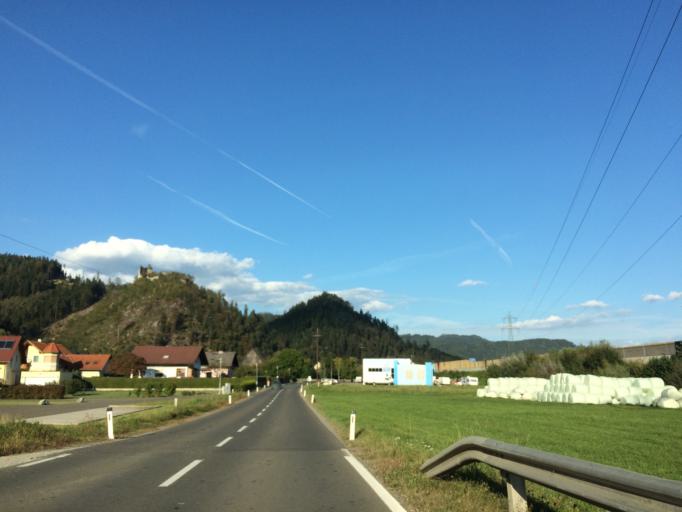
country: AT
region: Styria
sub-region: Politischer Bezirk Leoben
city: Sankt Michael in Obersteiermark
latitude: 47.3291
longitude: 14.9746
